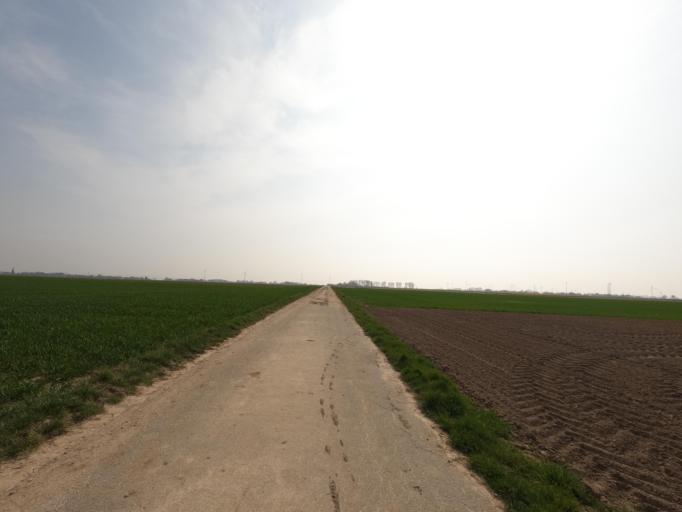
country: DE
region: North Rhine-Westphalia
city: Erkelenz
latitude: 51.0481
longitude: 6.3330
